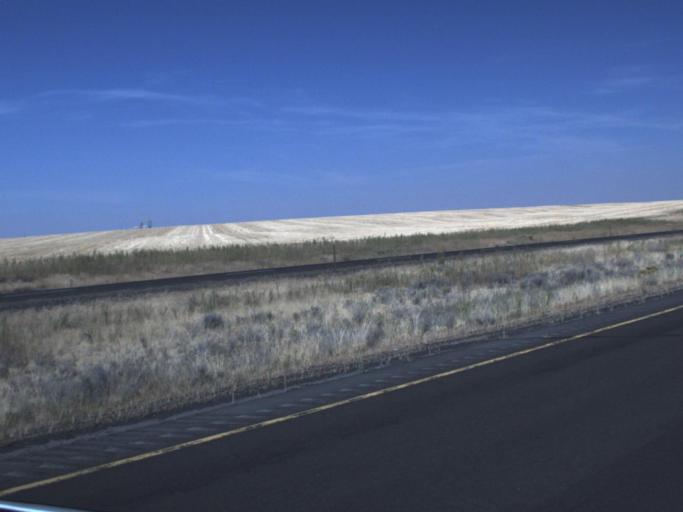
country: US
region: Washington
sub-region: Adams County
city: Ritzville
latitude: 47.1315
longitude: -118.3440
